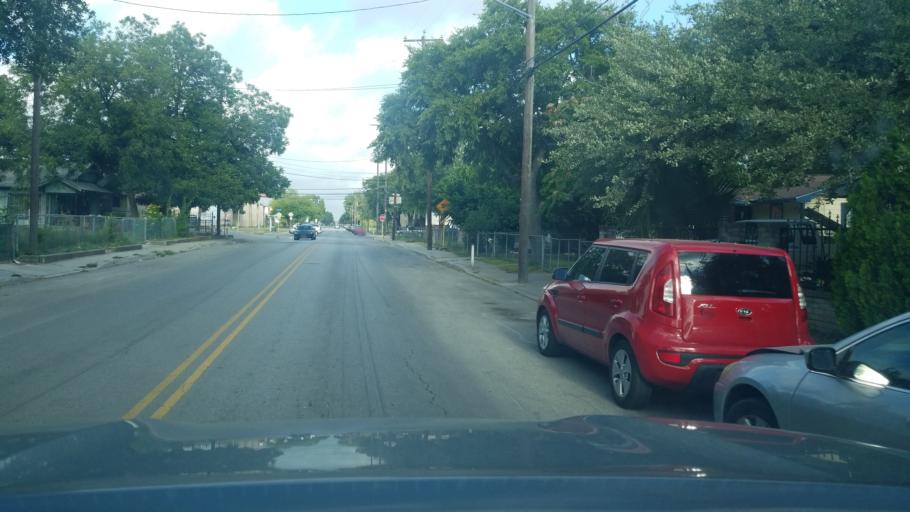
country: US
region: Texas
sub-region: Bexar County
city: San Antonio
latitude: 29.4115
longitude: -98.5326
